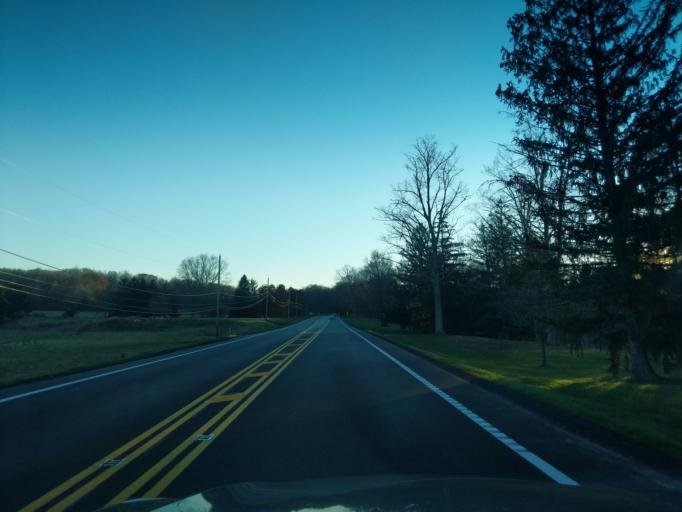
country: US
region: Ohio
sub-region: Licking County
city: Harbor Hills
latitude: 39.9819
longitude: -82.4096
